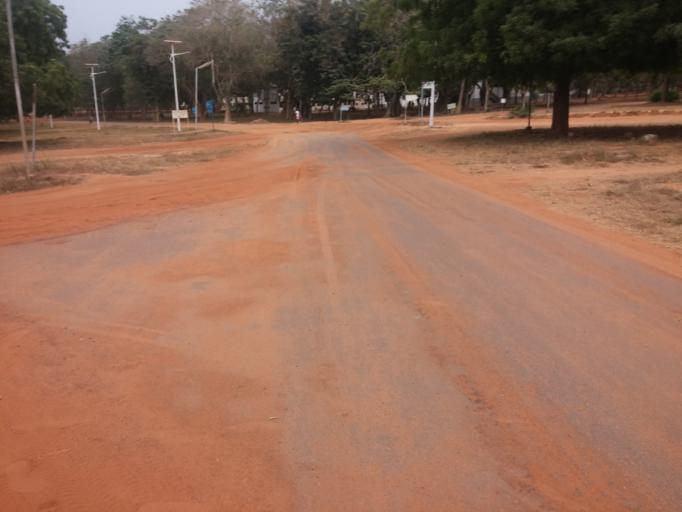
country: TG
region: Maritime
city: Lome
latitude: 6.1736
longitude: 1.2158
